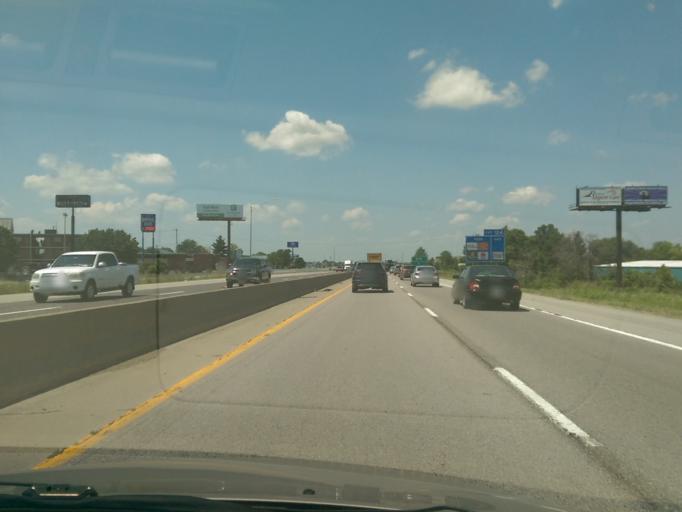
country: US
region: Missouri
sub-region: Boone County
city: Columbia
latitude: 38.9656
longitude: -92.3636
